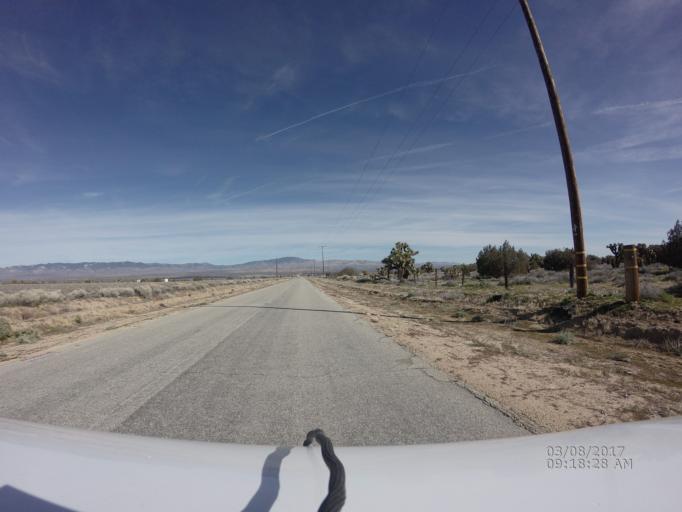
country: US
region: California
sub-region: Los Angeles County
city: Green Valley
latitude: 34.7871
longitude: -118.4666
